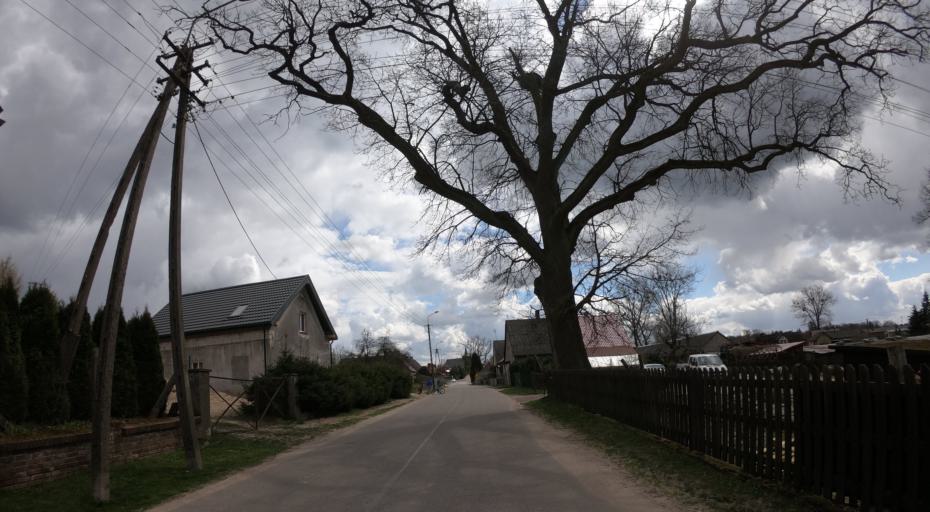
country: PL
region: West Pomeranian Voivodeship
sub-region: Powiat drawski
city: Drawsko Pomorskie
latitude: 53.5253
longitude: 15.8877
